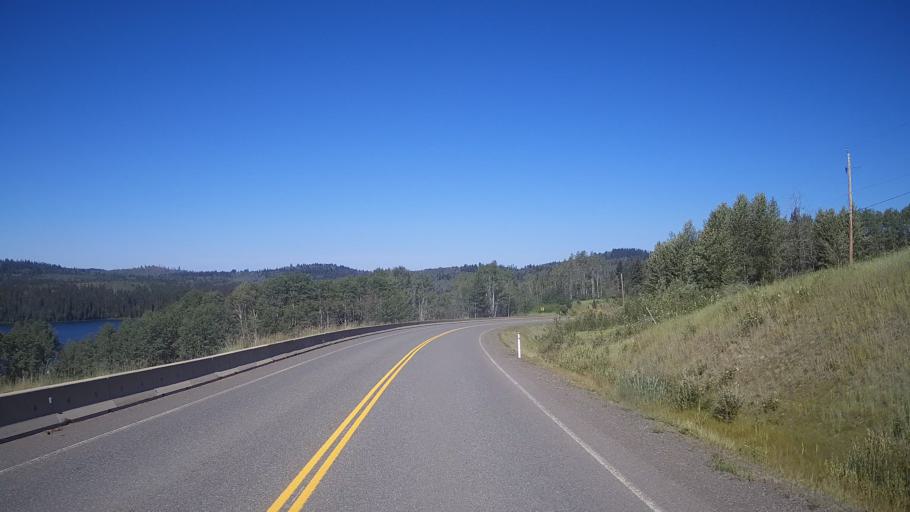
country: CA
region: British Columbia
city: Kamloops
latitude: 51.4990
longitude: -120.5954
